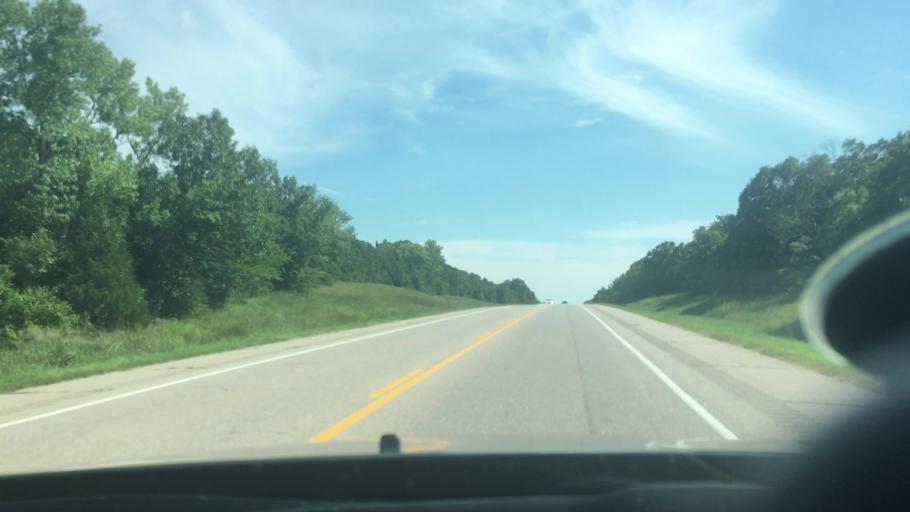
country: US
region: Oklahoma
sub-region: Seminole County
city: Maud
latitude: 35.1063
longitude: -96.6789
